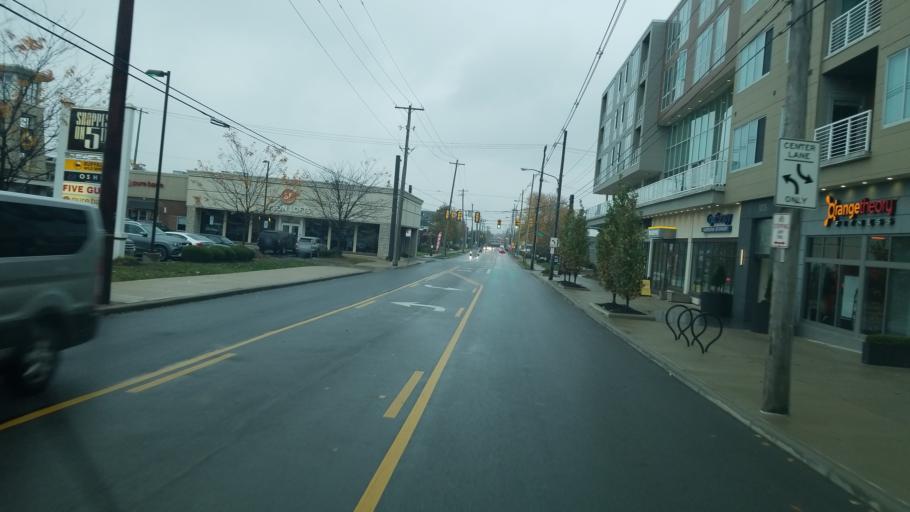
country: US
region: Ohio
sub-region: Franklin County
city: Grandview Heights
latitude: 39.9882
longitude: -83.0328
